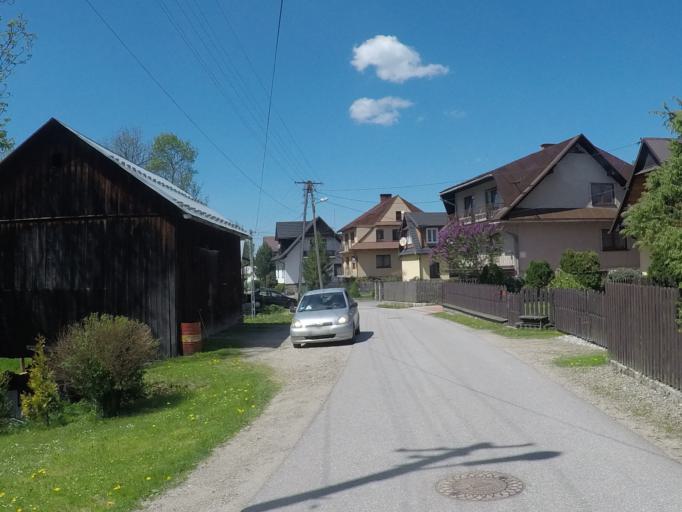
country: PL
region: Lesser Poland Voivodeship
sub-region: Powiat tatrzanski
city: Bukowina Tatrzanska
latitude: 49.3371
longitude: 20.1394
